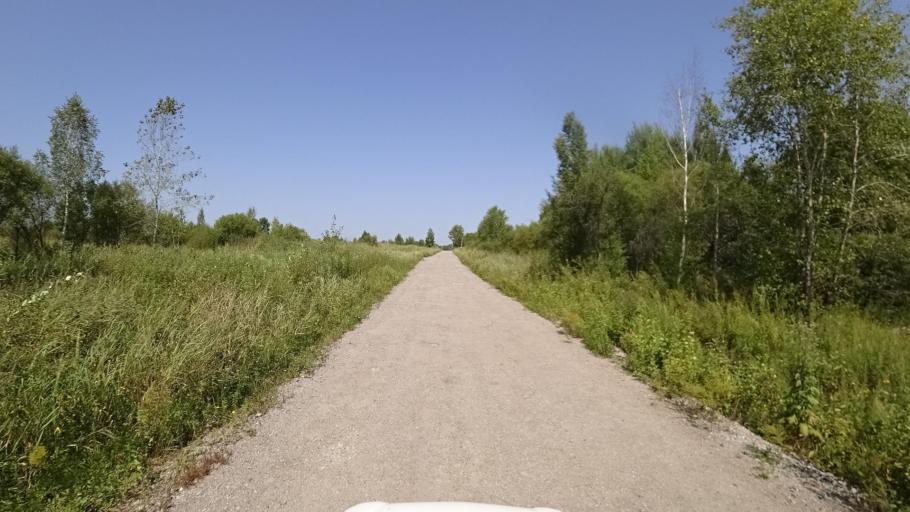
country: RU
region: Khabarovsk Krai
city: Khor
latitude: 47.9653
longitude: 135.1132
